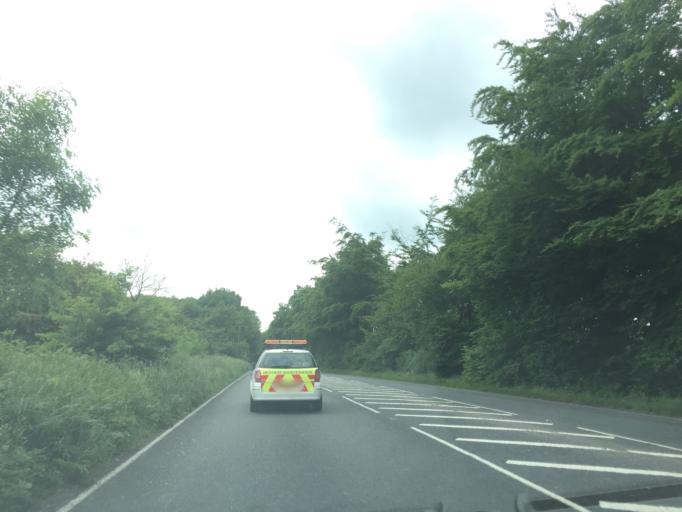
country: GB
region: England
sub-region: Hampshire
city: Four Marks
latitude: 51.1184
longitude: -1.0269
